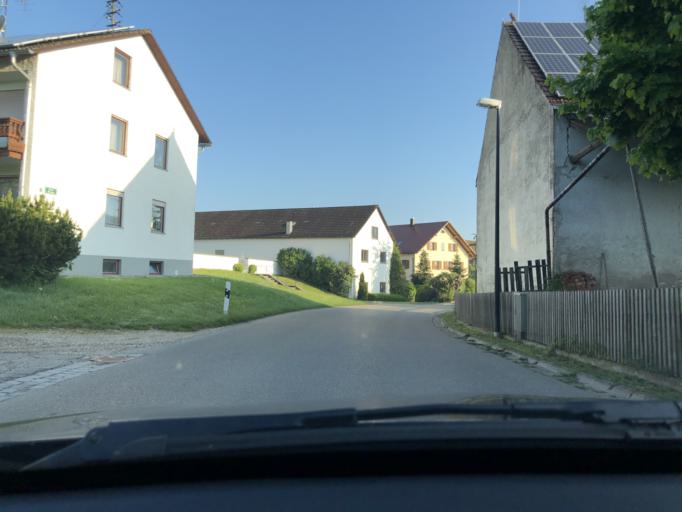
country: DE
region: Bavaria
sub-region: Upper Bavaria
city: Schweitenkirchen
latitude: 48.4855
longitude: 11.6281
